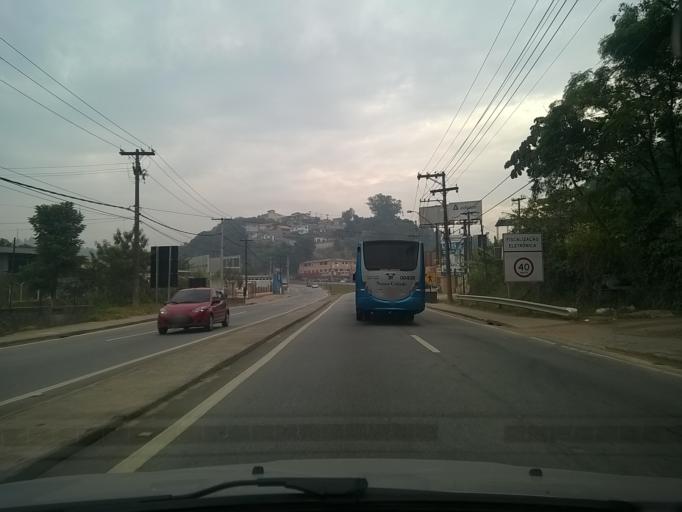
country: BR
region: Sao Paulo
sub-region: Franco Da Rocha
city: Franco da Rocha
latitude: -23.3276
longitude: -46.7510
